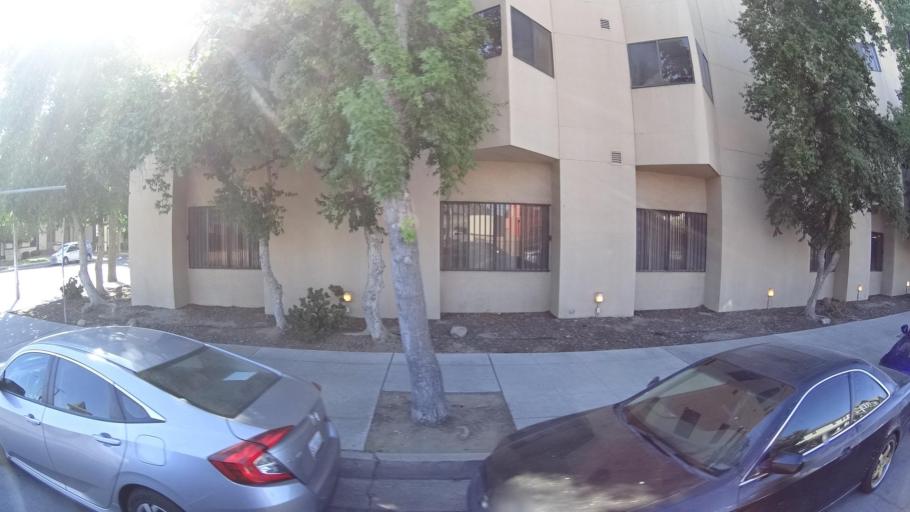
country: US
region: California
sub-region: Fresno County
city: Fresno
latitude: 36.7428
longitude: -119.7949
